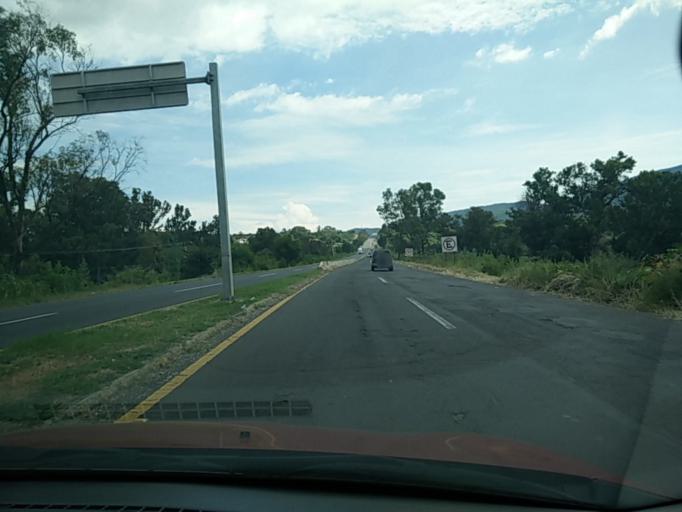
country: MX
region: Jalisco
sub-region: Ixtlahuacan de los Membrillos
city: Los Cedros
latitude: 20.3833
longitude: -103.2193
